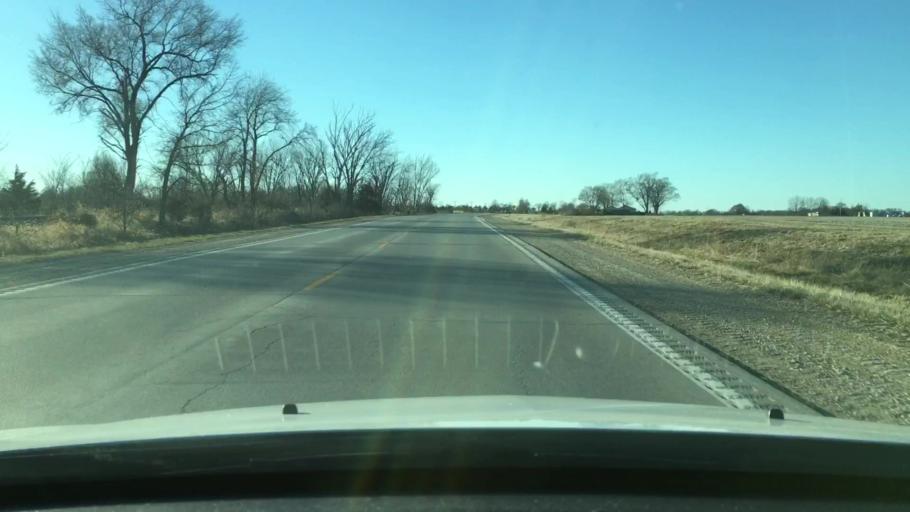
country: US
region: Missouri
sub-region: Audrain County
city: Mexico
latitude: 39.1910
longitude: -92.0053
